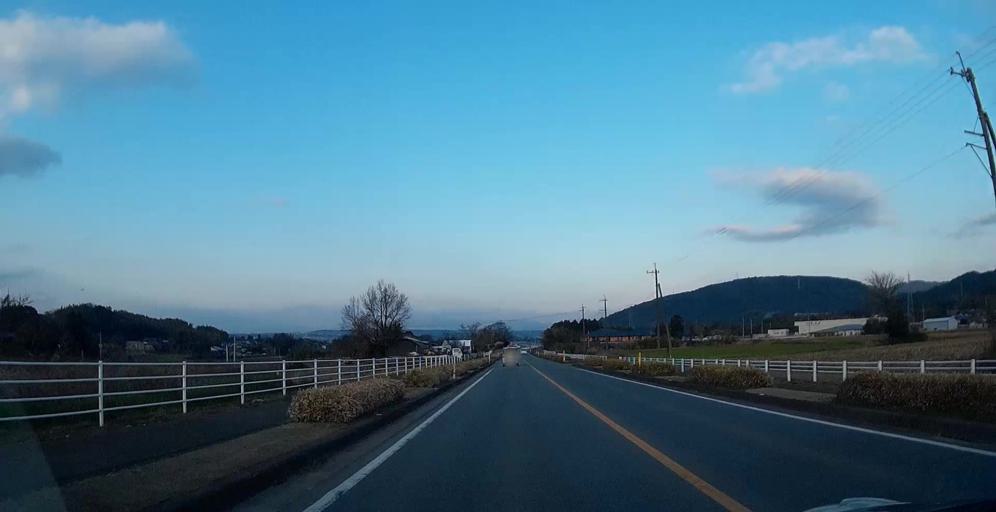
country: JP
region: Kumamoto
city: Kumamoto
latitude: 32.7510
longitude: 130.8014
